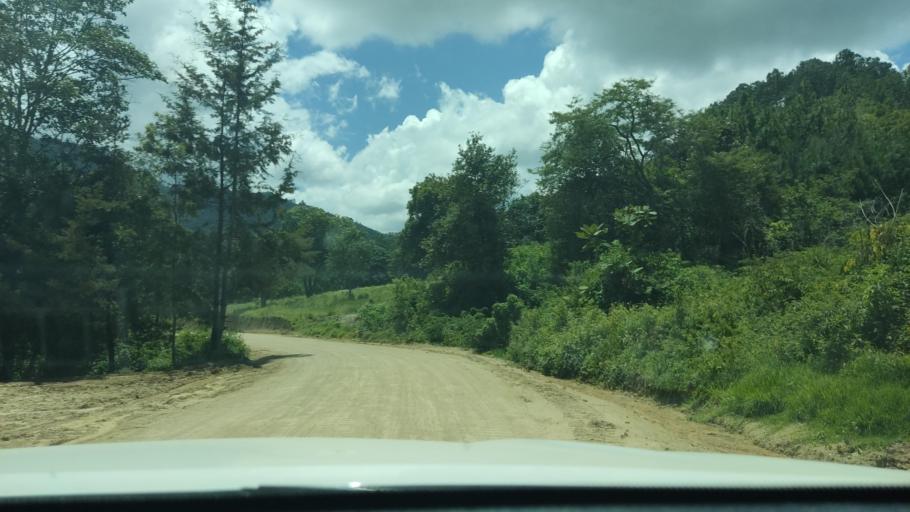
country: GT
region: Chimaltenango
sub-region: Municipio de San Juan Comalapa
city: Comalapa
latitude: 14.7644
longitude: -90.8827
